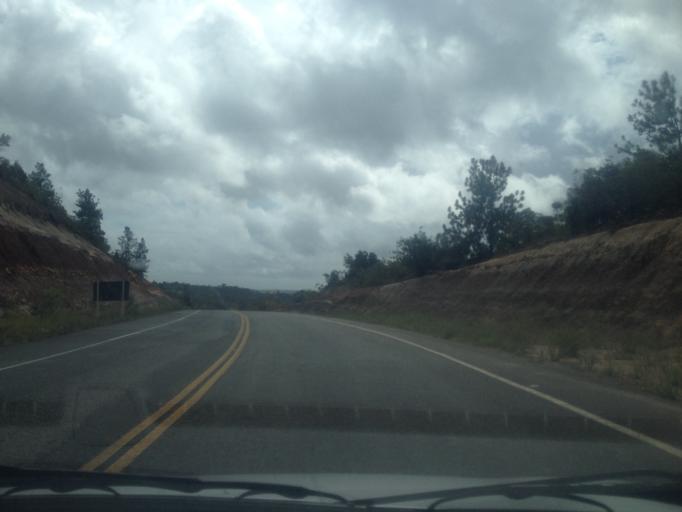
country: BR
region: Bahia
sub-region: Conde
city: Conde
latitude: -12.0952
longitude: -37.7728
